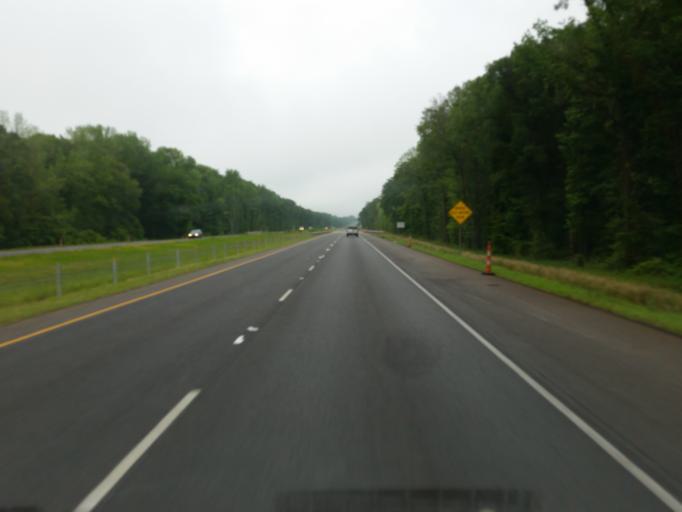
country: US
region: Louisiana
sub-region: Bienville Parish
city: Arcadia
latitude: 32.5630
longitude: -93.1004
